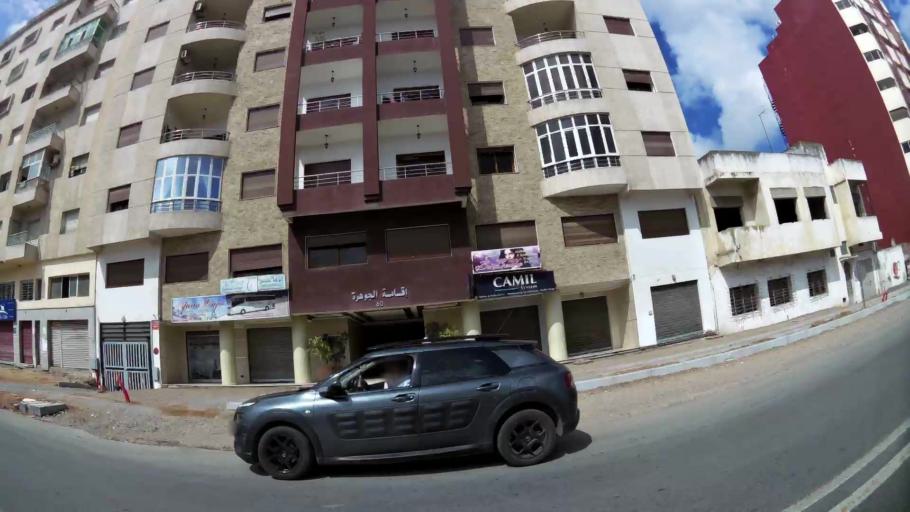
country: MA
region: Gharb-Chrarda-Beni Hssen
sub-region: Kenitra Province
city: Kenitra
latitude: 34.2603
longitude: -6.5778
